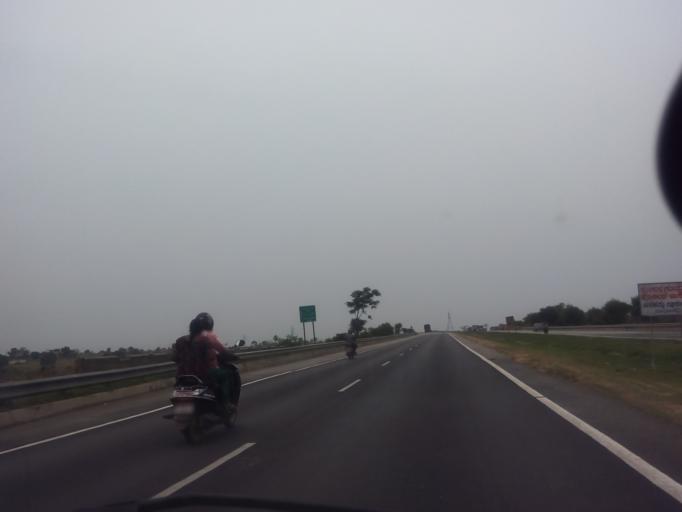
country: IN
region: Karnataka
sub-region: Bangalore Urban
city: Bangalore
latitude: 12.9072
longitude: 77.4686
